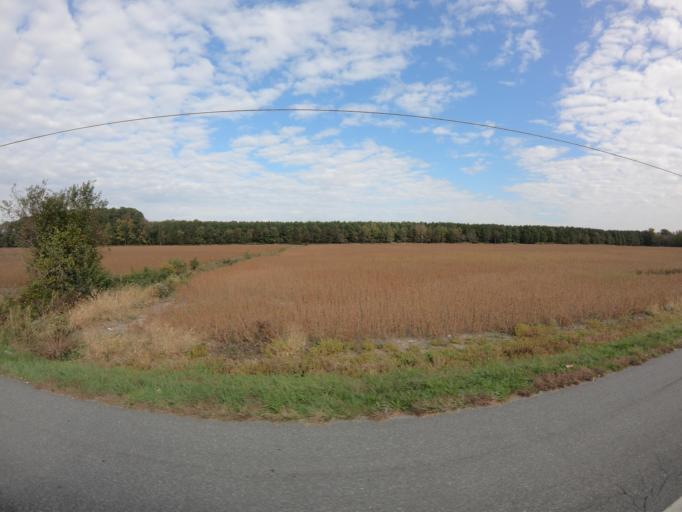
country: US
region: Delaware
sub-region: Sussex County
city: Georgetown
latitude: 38.6987
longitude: -75.4245
